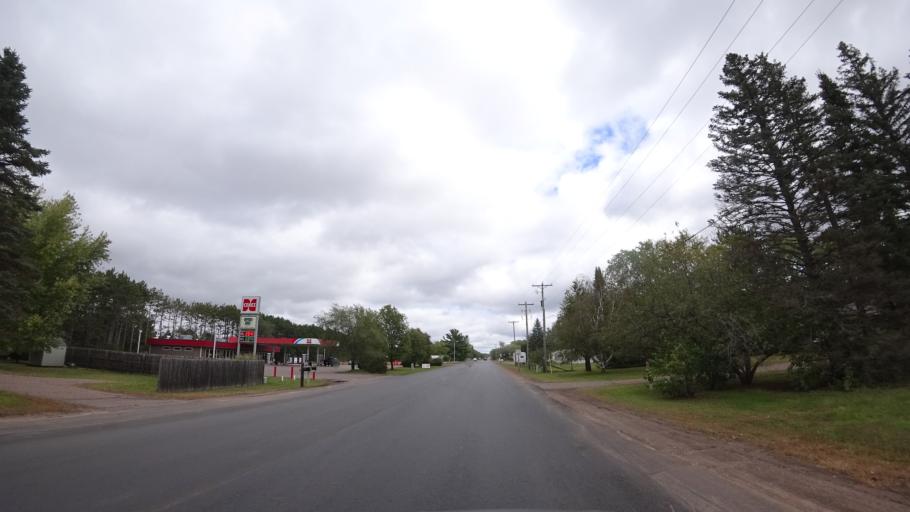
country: US
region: Wisconsin
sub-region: Chippewa County
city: Lake Wissota
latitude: 44.9296
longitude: -91.2739
